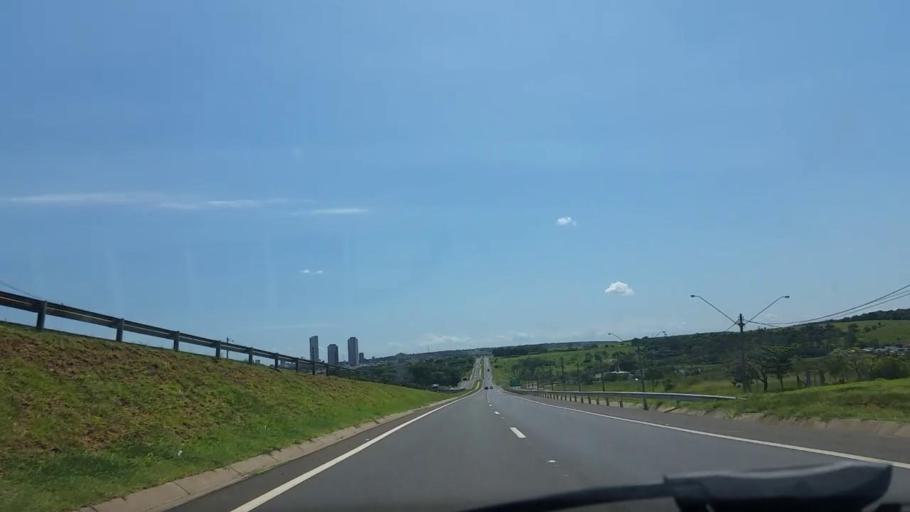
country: BR
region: Sao Paulo
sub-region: Bauru
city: Bauru
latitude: -22.3902
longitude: -49.0772
